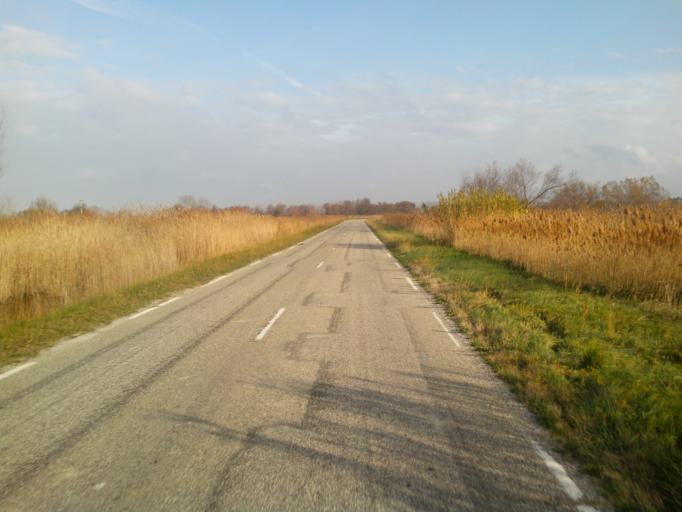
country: FR
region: Provence-Alpes-Cote d'Azur
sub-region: Departement des Bouches-du-Rhone
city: Arles
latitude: 43.5724
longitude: 4.5461
